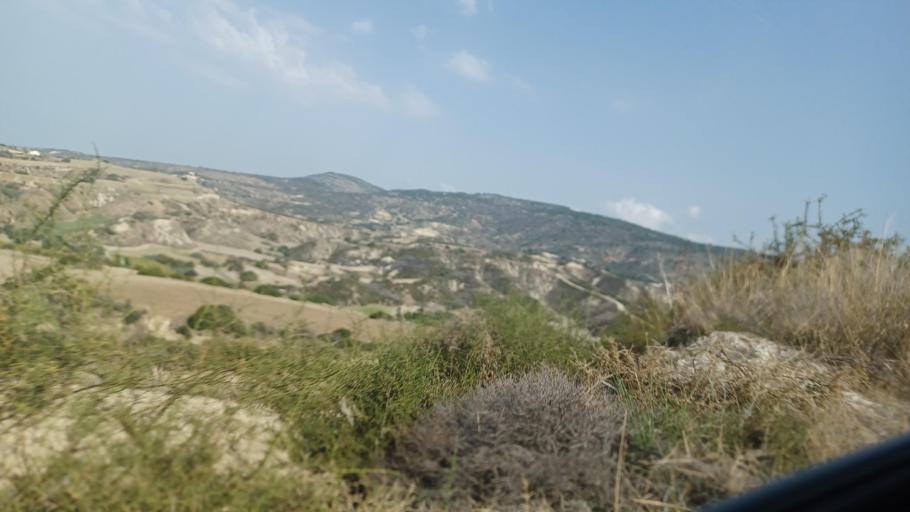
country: CY
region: Pafos
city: Polis
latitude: 34.9920
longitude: 32.4566
